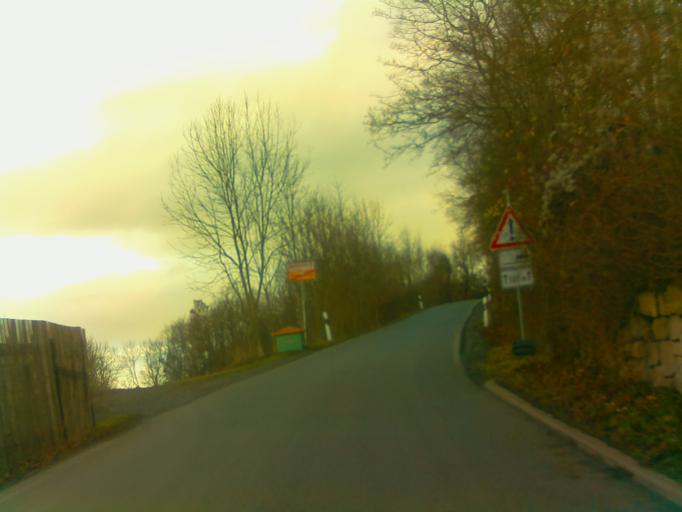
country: DE
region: Thuringia
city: Rudolstadt
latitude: 50.6930
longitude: 11.3415
